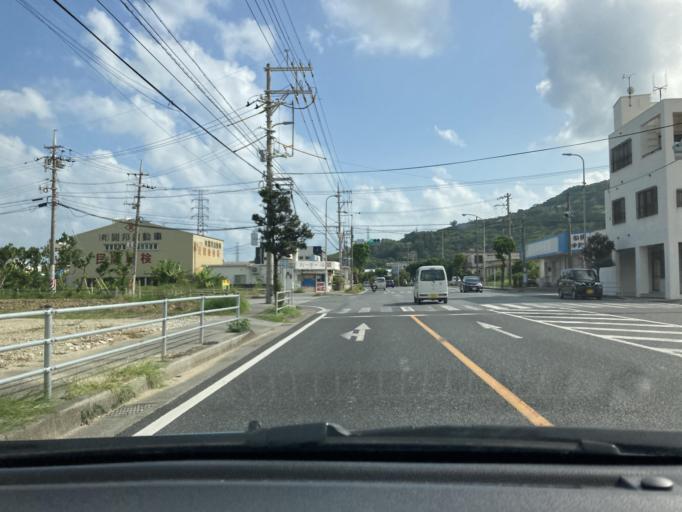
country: JP
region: Okinawa
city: Okinawa
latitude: 26.2954
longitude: 127.8091
